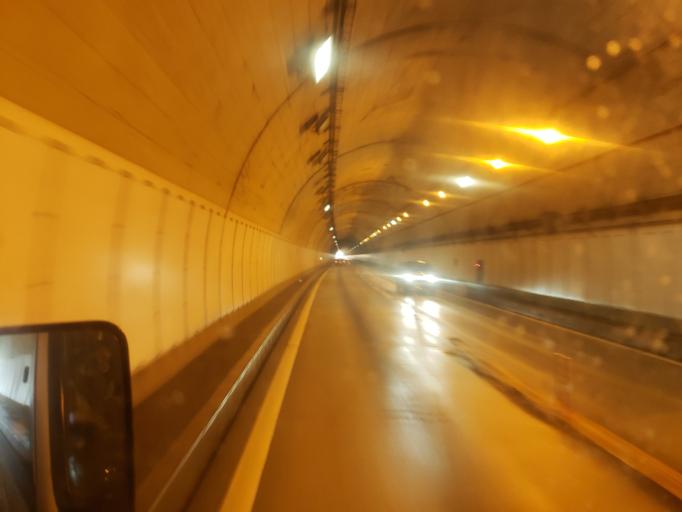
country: JP
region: Hyogo
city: Nishiwaki
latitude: 35.1640
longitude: 134.7862
